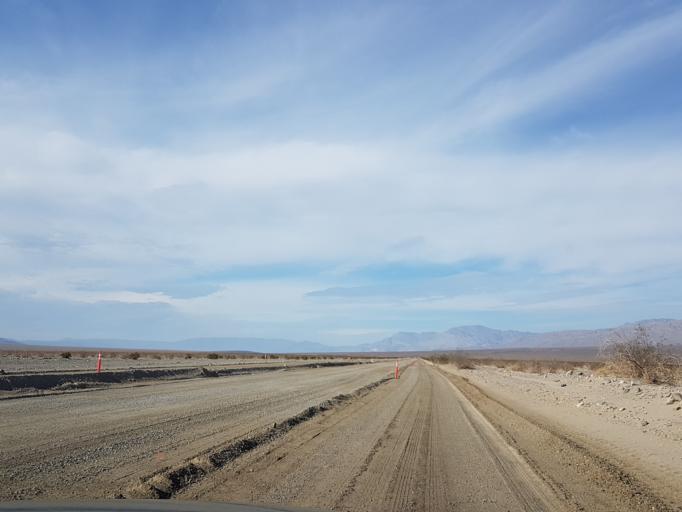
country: US
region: California
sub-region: San Bernardino County
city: Searles Valley
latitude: 36.1435
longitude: -117.2965
